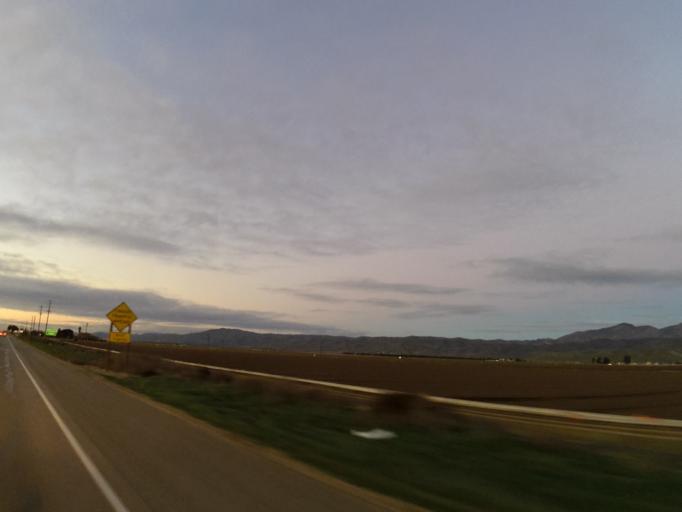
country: US
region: California
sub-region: Monterey County
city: Greenfield
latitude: 36.3502
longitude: -121.2652
